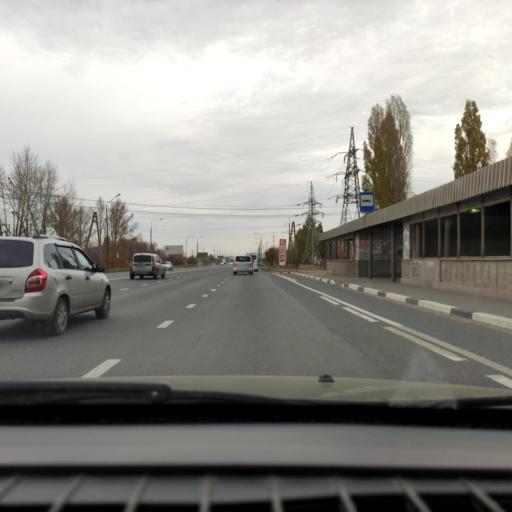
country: RU
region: Samara
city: Tol'yatti
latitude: 53.5563
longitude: 49.2885
